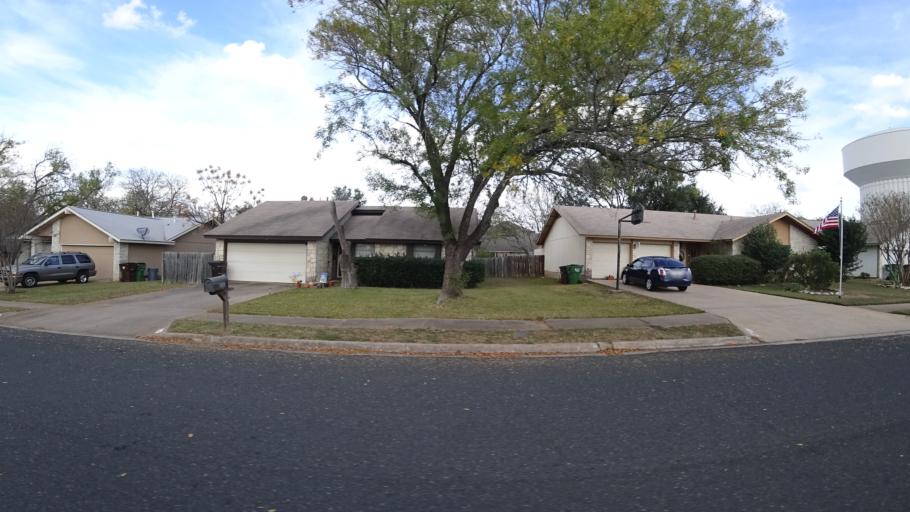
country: US
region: Texas
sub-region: Williamson County
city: Brushy Creek
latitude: 30.5114
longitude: -97.7316
